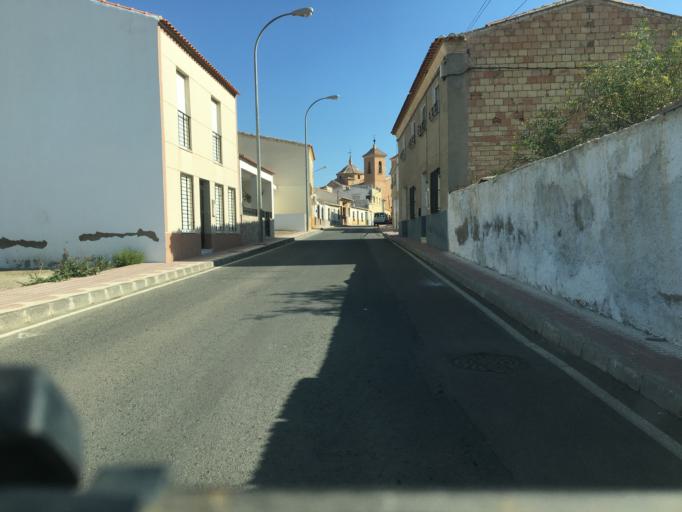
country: ES
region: Andalusia
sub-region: Provincia de Almeria
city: Huercal-Overa
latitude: 37.4607
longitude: -1.9894
